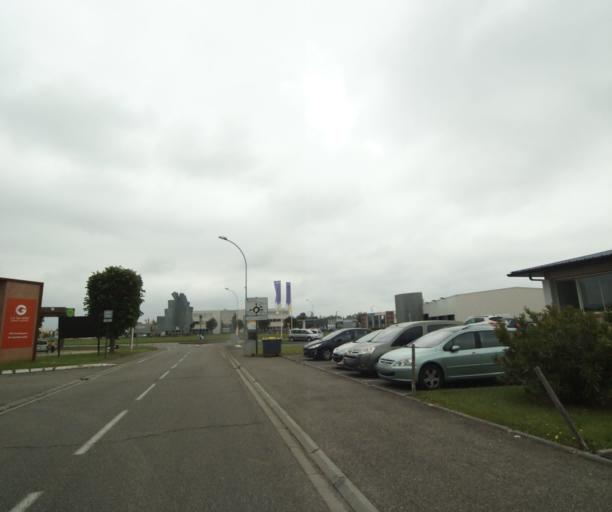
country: FR
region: Midi-Pyrenees
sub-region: Departement du Tarn-et-Garonne
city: Bressols
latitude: 43.9896
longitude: 1.3310
